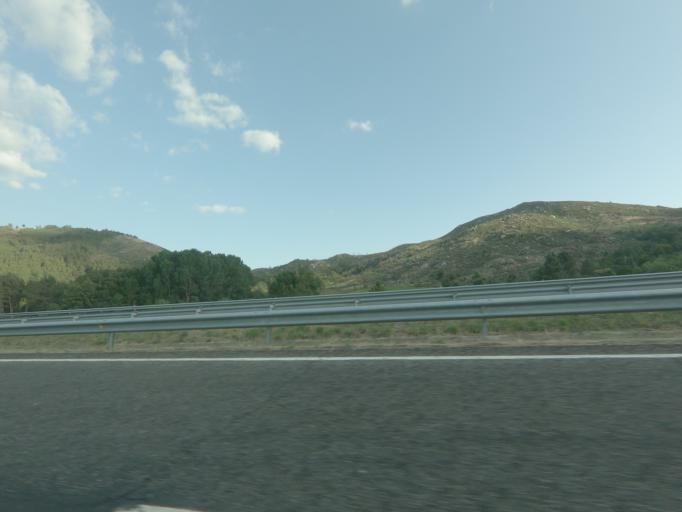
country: ES
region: Galicia
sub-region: Provincia de Ourense
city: Oimbra
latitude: 41.9227
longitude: -7.4779
